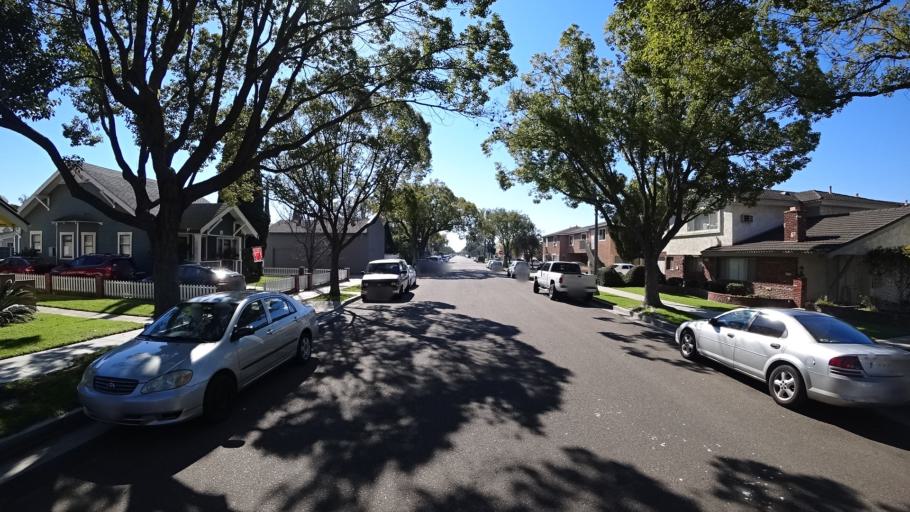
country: US
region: California
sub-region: Orange County
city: Anaheim
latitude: 33.8351
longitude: -117.9085
